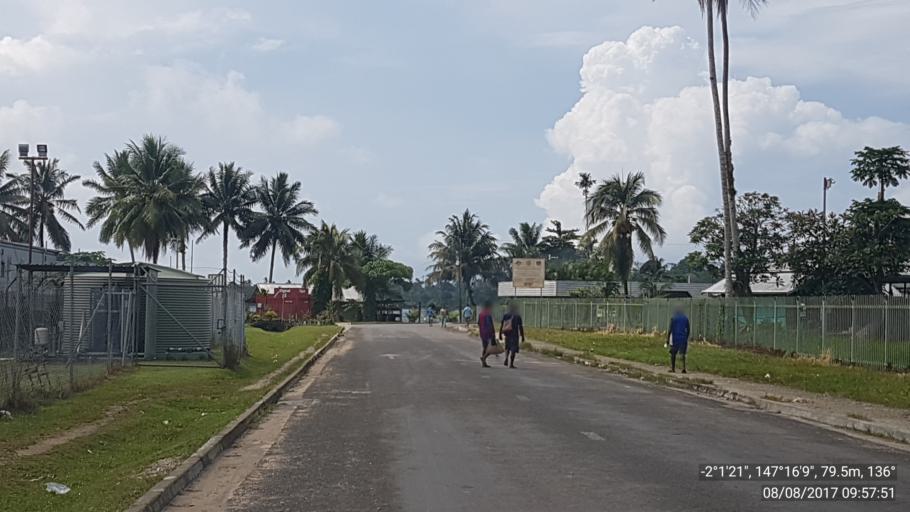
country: PG
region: Manus
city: Lorengau
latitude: -2.0228
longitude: 147.2693
